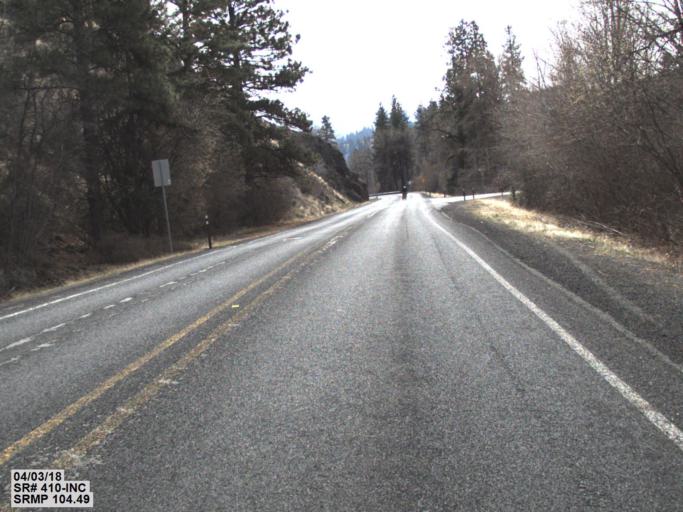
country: US
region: Washington
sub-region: Yakima County
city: Tieton
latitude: 46.8580
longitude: -120.9528
